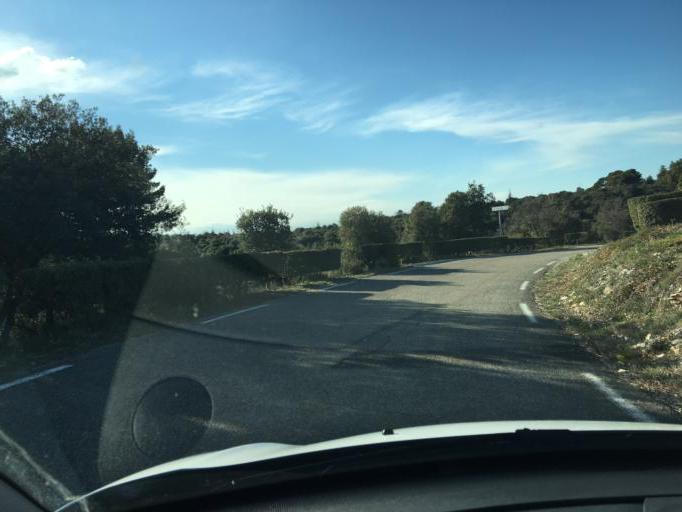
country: FR
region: Provence-Alpes-Cote d'Azur
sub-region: Departement du Vaucluse
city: Villes-sur-Auzon
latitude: 44.0423
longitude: 5.2554
